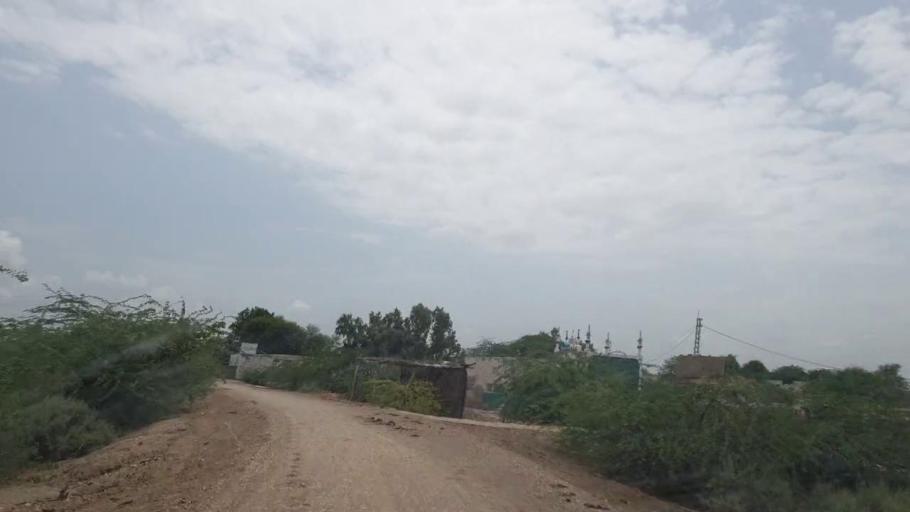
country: PK
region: Sindh
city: Naukot
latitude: 24.9071
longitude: 69.2009
